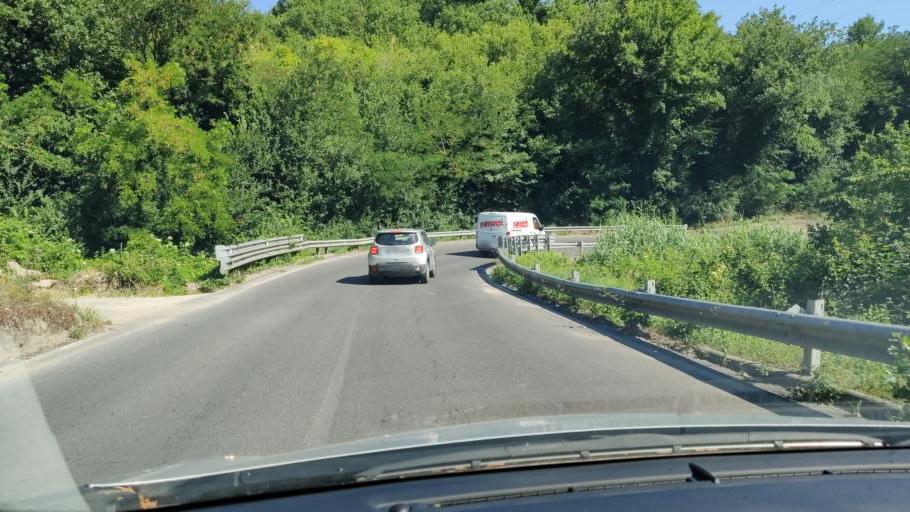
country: IT
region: Umbria
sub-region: Provincia di Perugia
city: Todi
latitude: 42.7842
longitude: 12.4146
